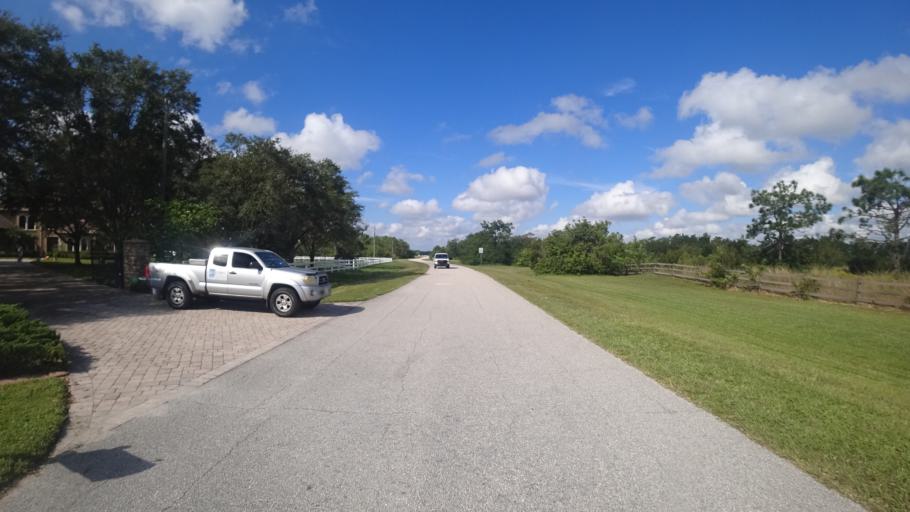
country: US
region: Florida
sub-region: Sarasota County
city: The Meadows
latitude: 27.4022
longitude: -82.3254
